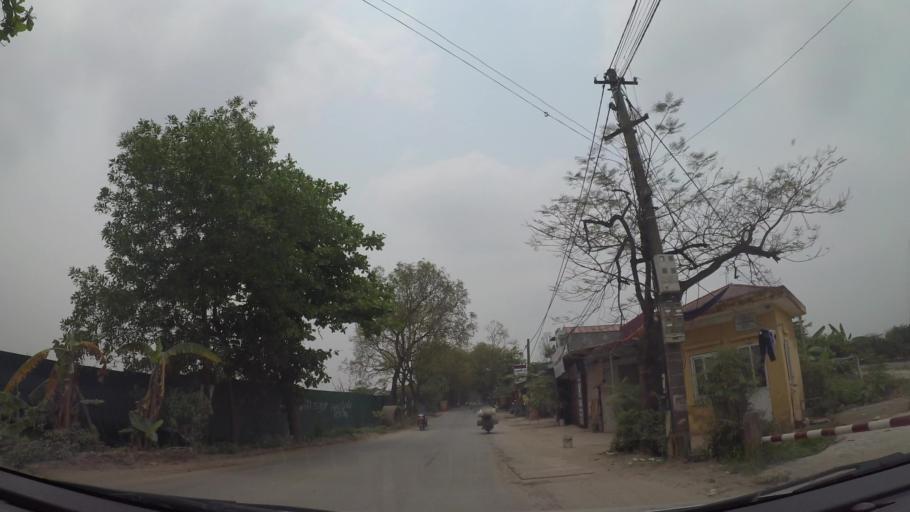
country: VN
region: Ha Noi
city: Cau Dien
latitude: 21.0195
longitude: 105.7440
